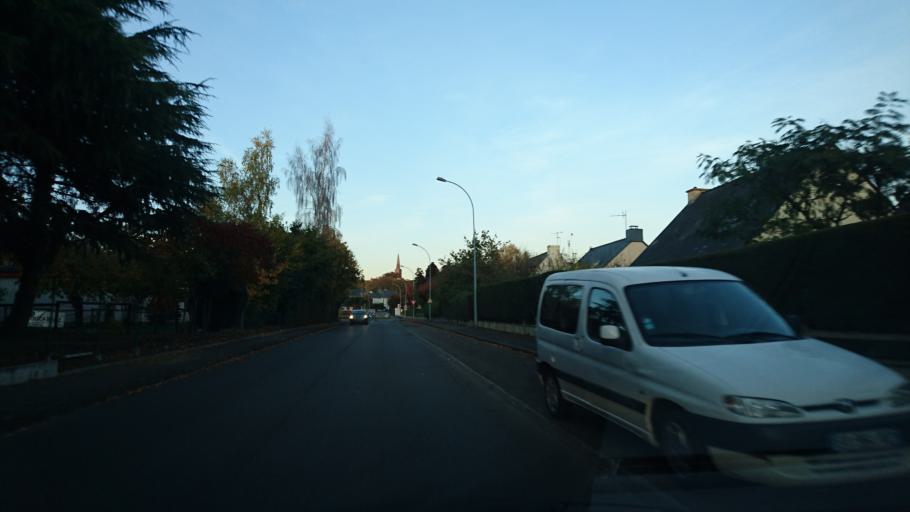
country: FR
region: Brittany
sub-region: Departement d'Ille-et-Vilaine
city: Bruz
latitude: 48.0202
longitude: -1.7528
